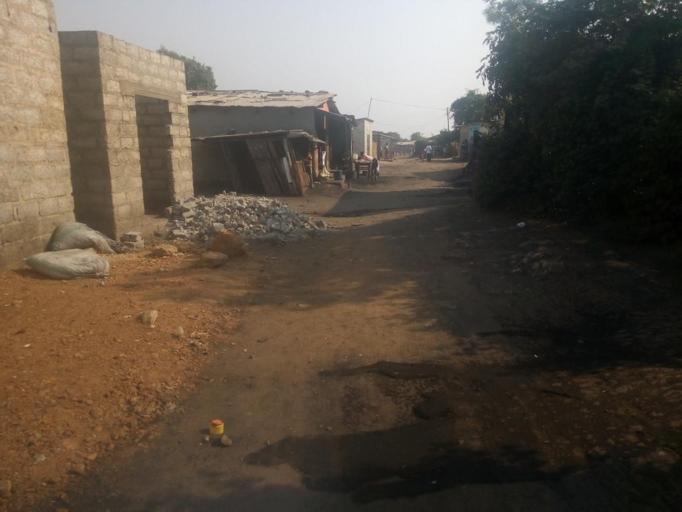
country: ZM
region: Lusaka
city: Lusaka
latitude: -15.4092
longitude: 28.3622
